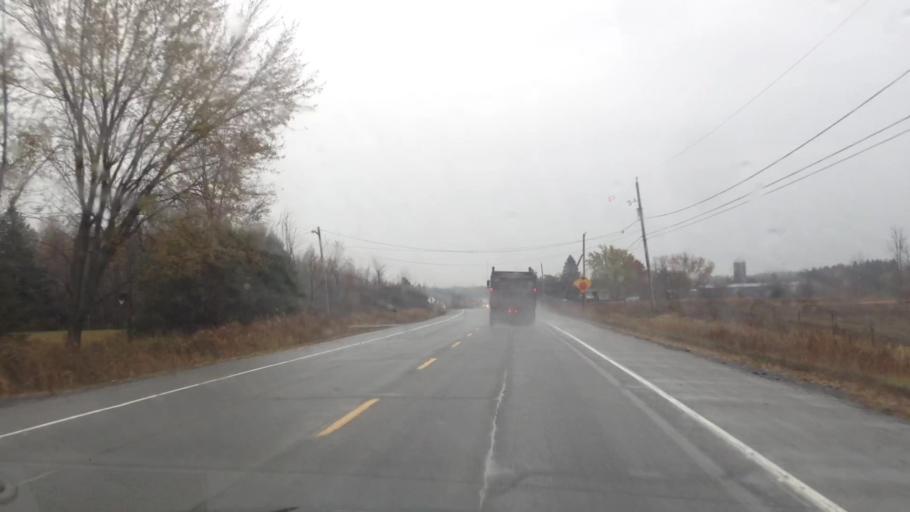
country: CA
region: Ontario
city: Clarence-Rockland
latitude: 45.3752
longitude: -75.3816
